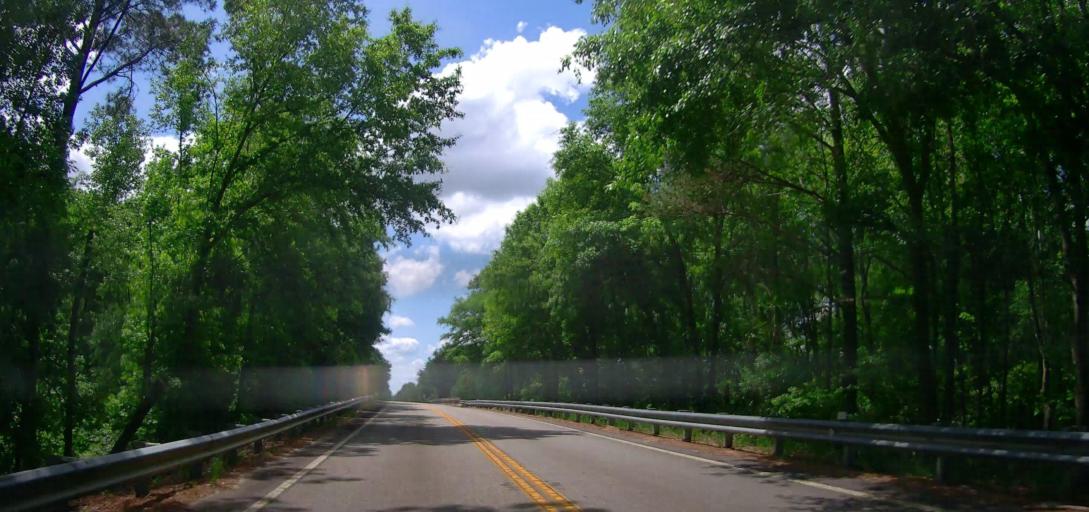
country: US
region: Georgia
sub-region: Dodge County
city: Chester
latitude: 32.5532
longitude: -83.1766
